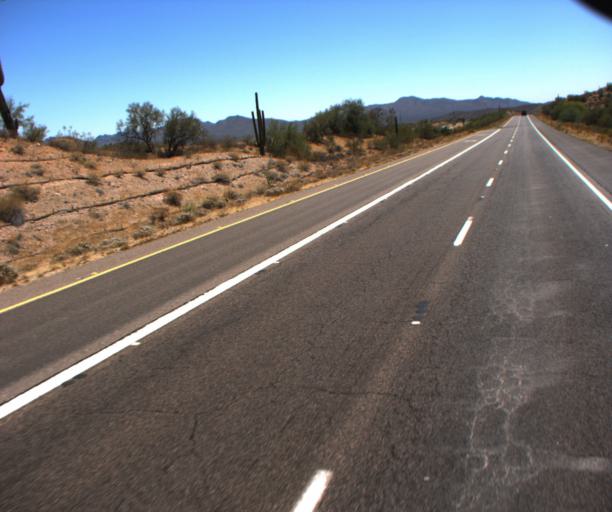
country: US
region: Arizona
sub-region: Maricopa County
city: Fountain Hills
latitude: 33.6016
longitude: -111.5873
